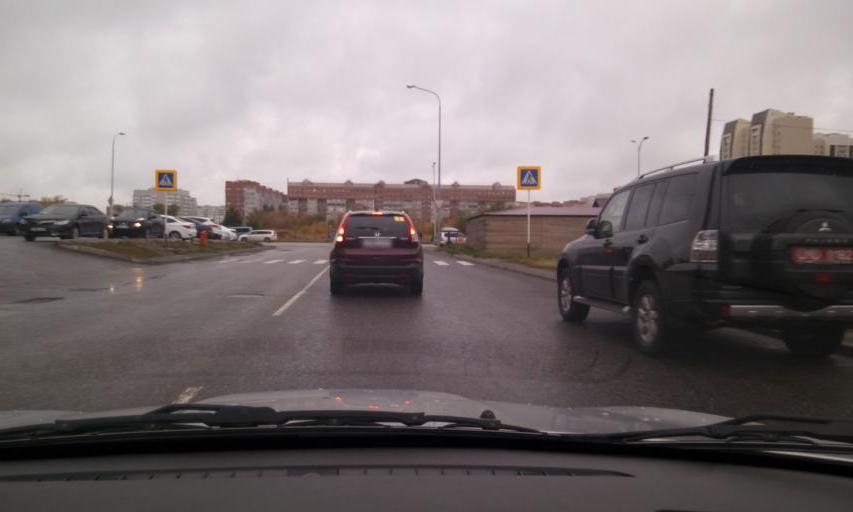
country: KZ
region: Astana Qalasy
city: Astana
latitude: 51.1615
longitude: 71.4028
